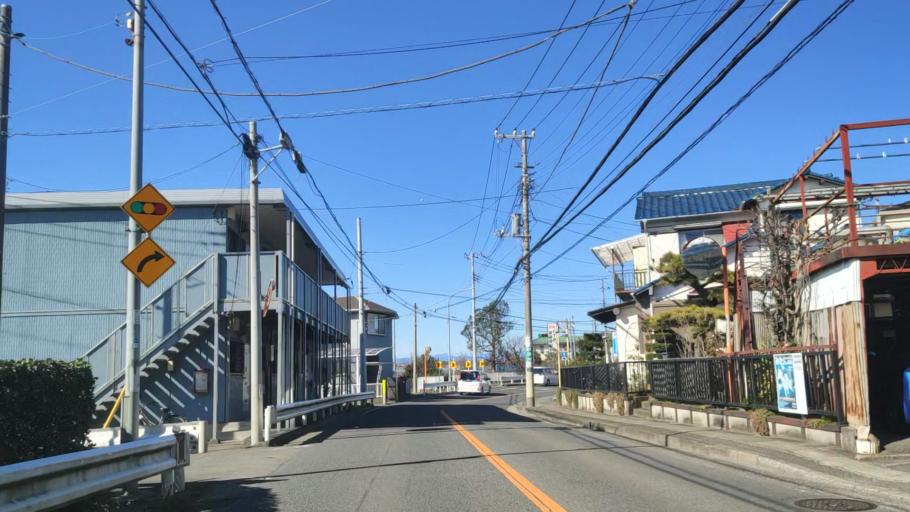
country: JP
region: Tokyo
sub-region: Machida-shi
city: Machida
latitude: 35.5214
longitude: 139.5357
